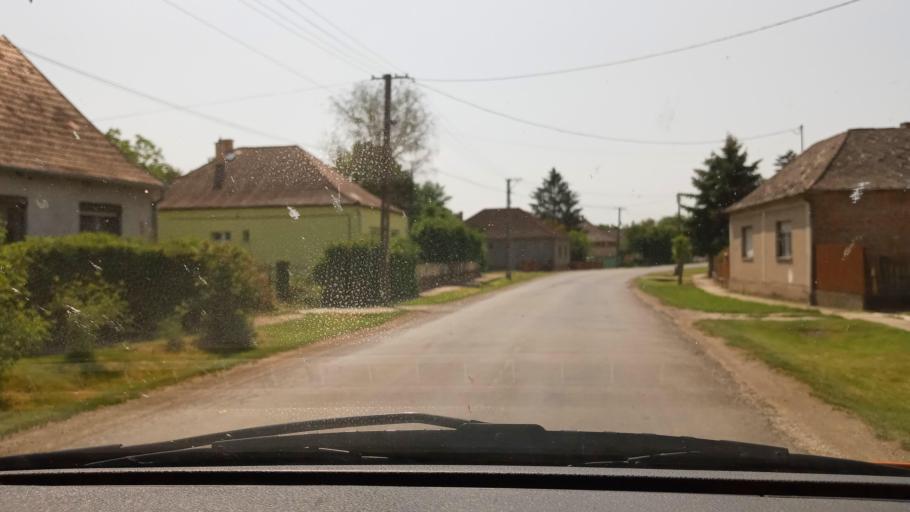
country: HU
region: Baranya
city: Szentlorinc
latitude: 46.0114
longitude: 18.0411
